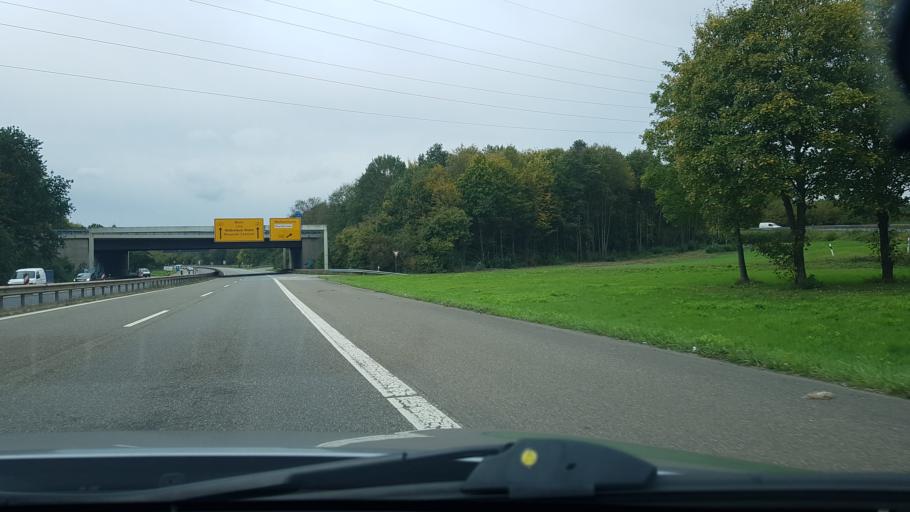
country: DE
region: Rheinland-Pfalz
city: Neuwied
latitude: 50.4414
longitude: 7.4869
